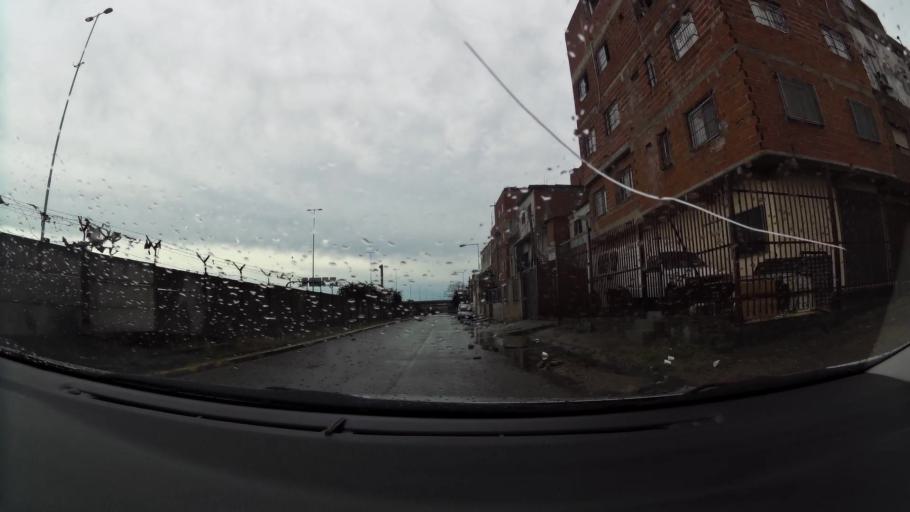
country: AR
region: Buenos Aires F.D.
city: Villa Lugano
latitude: -34.6588
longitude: -58.4576
